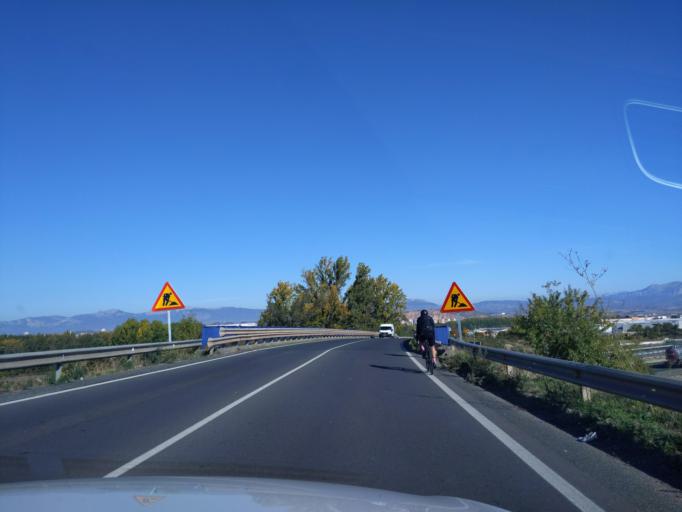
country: ES
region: La Rioja
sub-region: Provincia de La Rioja
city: Villamediana de Iregua
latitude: 42.4407
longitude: -2.4187
